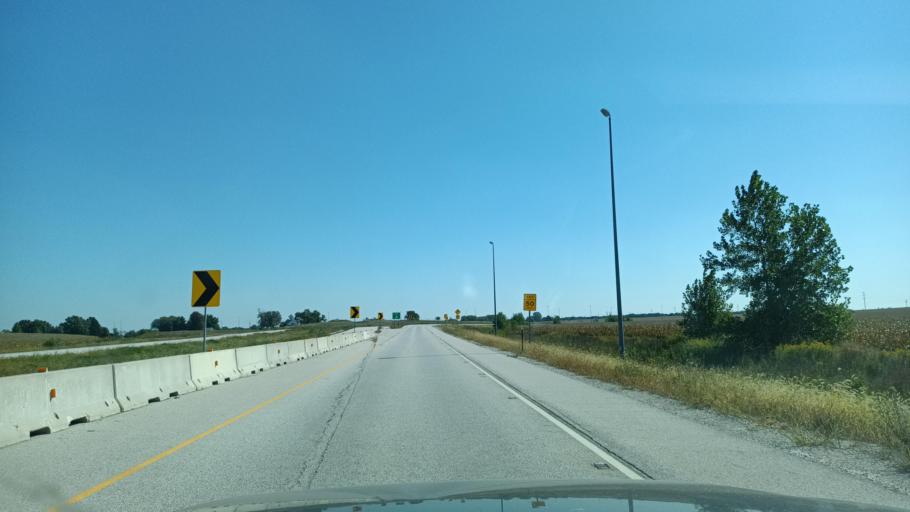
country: US
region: Illinois
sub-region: McDonough County
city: Macomb
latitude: 40.5031
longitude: -90.6809
